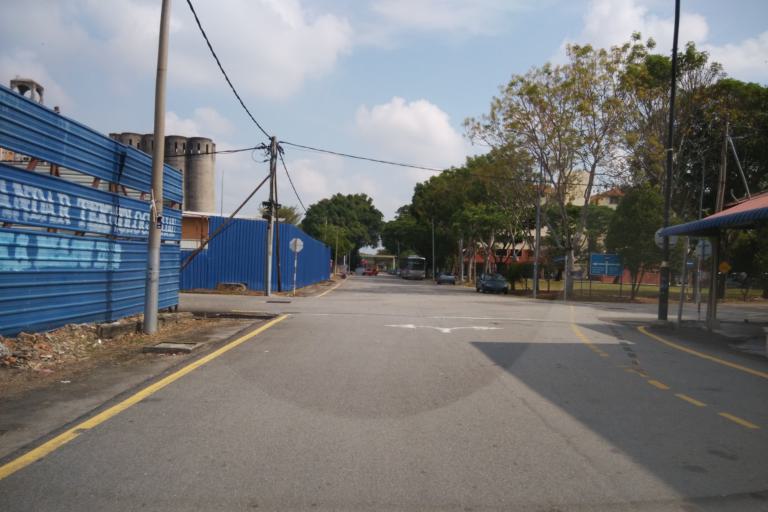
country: MY
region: Melaka
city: Malacca
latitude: 2.2045
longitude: 102.2492
